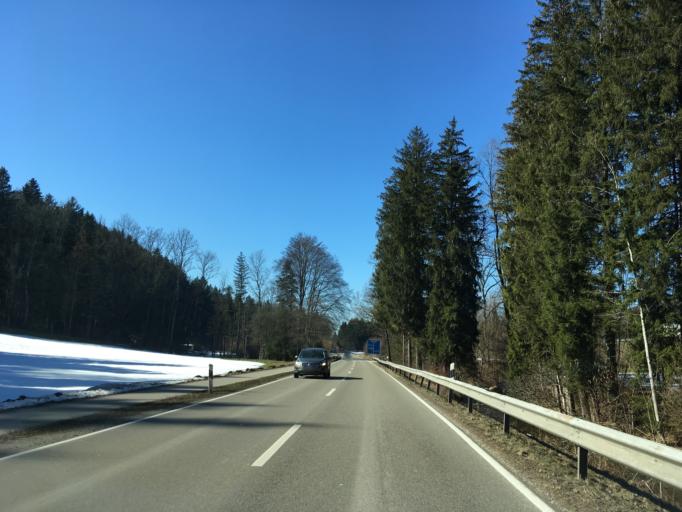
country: DE
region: Bavaria
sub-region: Upper Bavaria
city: Samerberg
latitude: 47.7957
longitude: 12.2194
